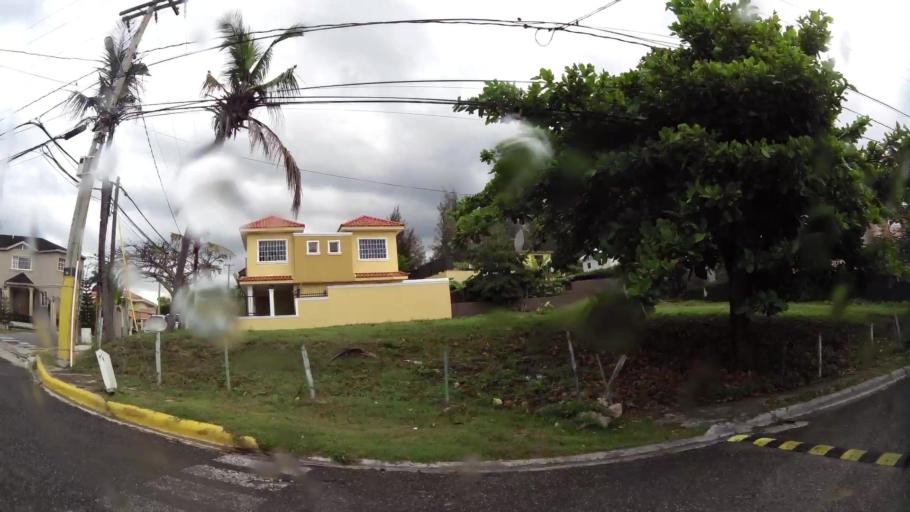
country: DO
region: Nacional
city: La Agustina
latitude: 18.5128
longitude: -69.9349
